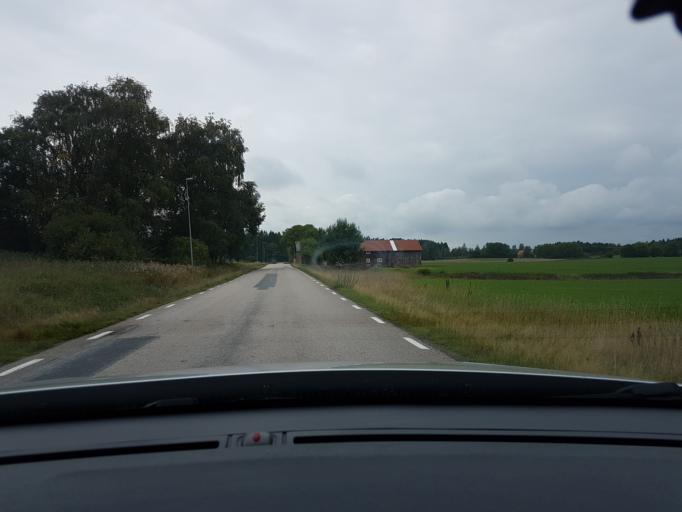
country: SE
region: Vaestra Goetaland
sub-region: Ale Kommun
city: Alvangen
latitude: 57.9167
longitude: 12.1411
